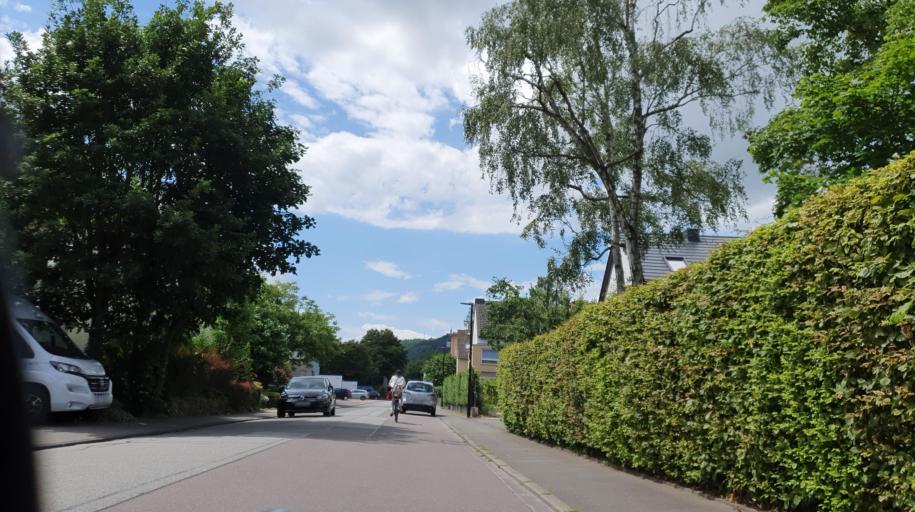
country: DE
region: Rheinland-Pfalz
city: Trier
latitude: 49.7681
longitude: 6.6449
